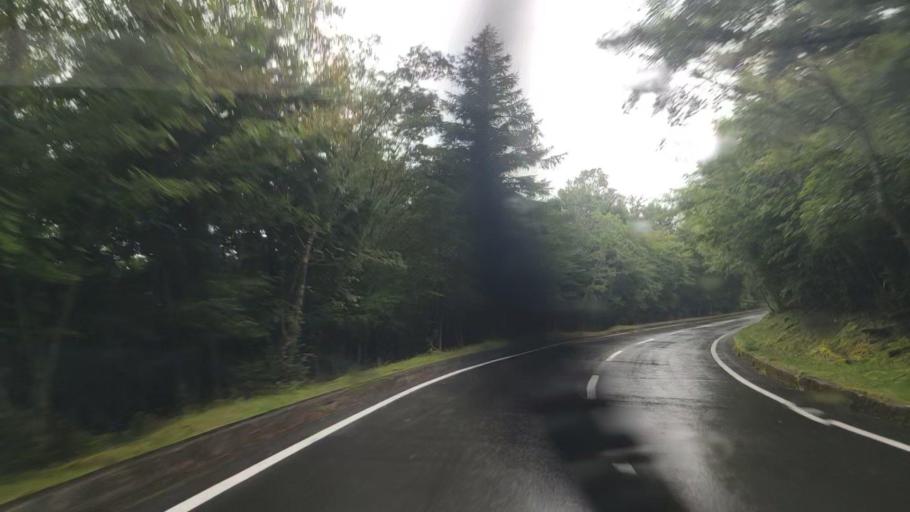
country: JP
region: Shizuoka
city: Fujinomiya
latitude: 35.3206
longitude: 138.7218
